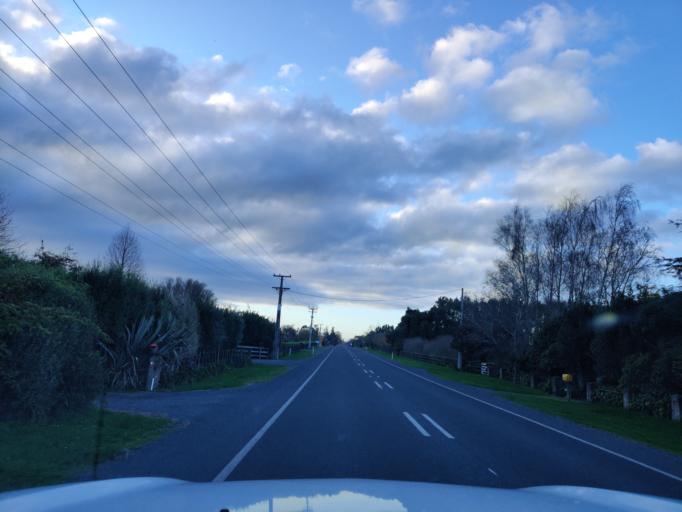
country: NZ
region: Waikato
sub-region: Waipa District
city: Cambridge
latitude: -37.8633
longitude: 175.4390
